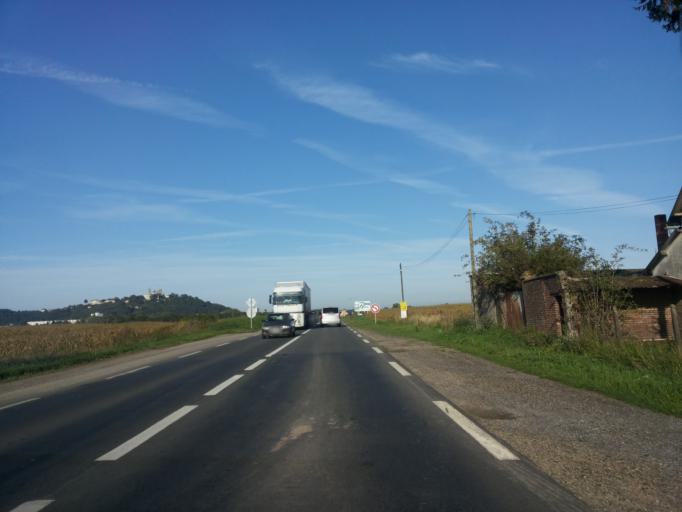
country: FR
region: Picardie
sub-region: Departement de l'Aisne
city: Athies-sous-Laon
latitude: 49.5659
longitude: 3.6668
